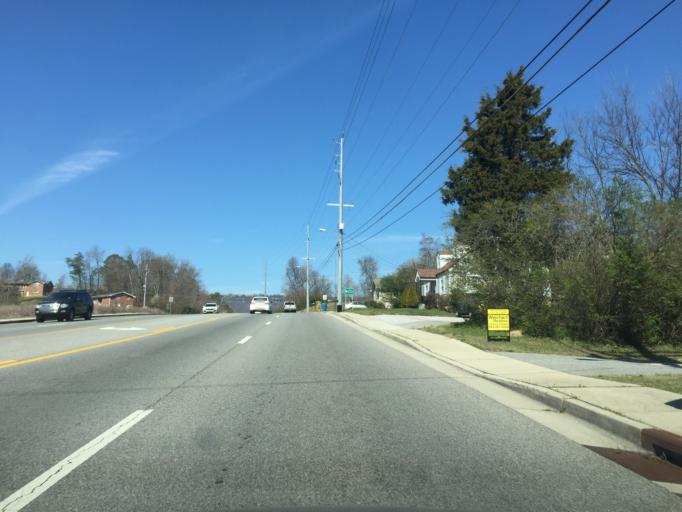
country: US
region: Tennessee
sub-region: Hamilton County
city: Red Bank
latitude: 35.1186
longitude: -85.2804
